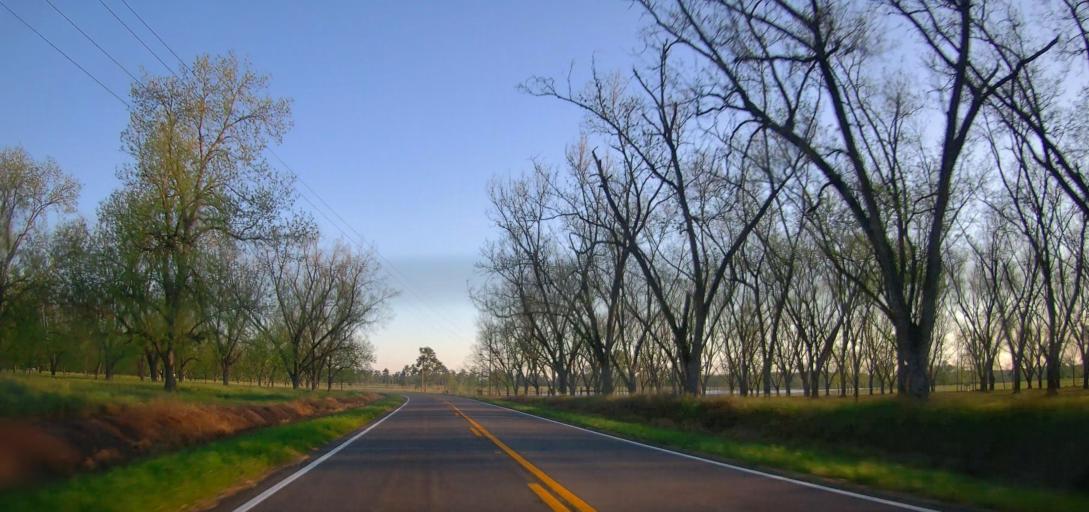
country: US
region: Georgia
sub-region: Irwin County
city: Ocilla
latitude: 31.6349
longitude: -83.2754
